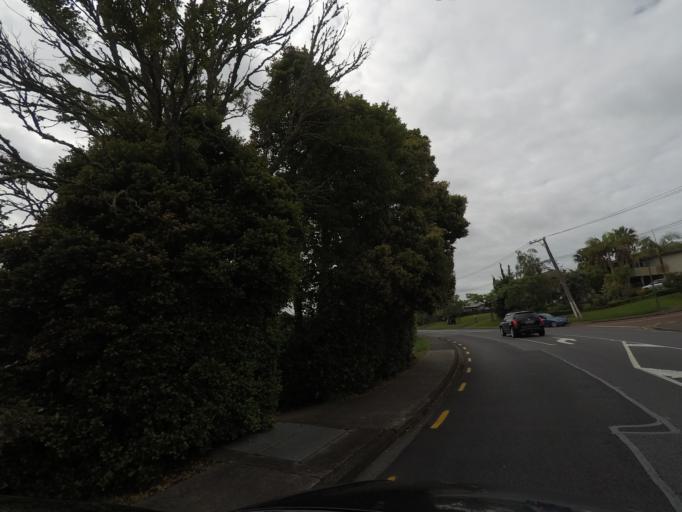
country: NZ
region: Auckland
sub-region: Auckland
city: Rosebank
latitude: -36.8527
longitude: 174.6101
